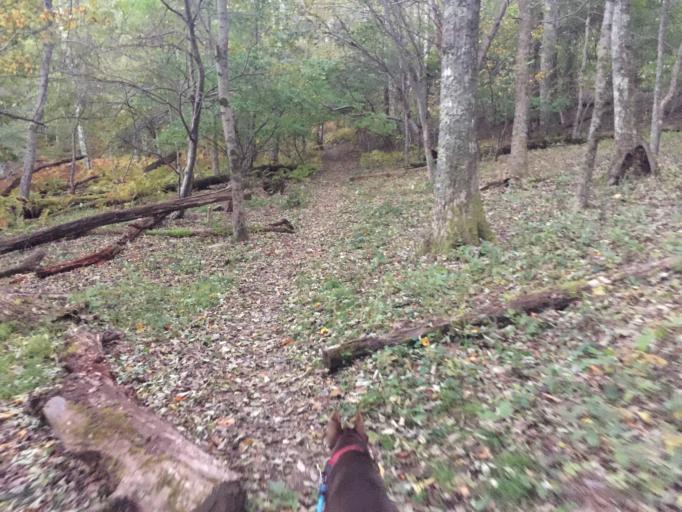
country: US
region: Virginia
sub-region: Page County
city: Stanley
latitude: 38.4358
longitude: -78.4771
